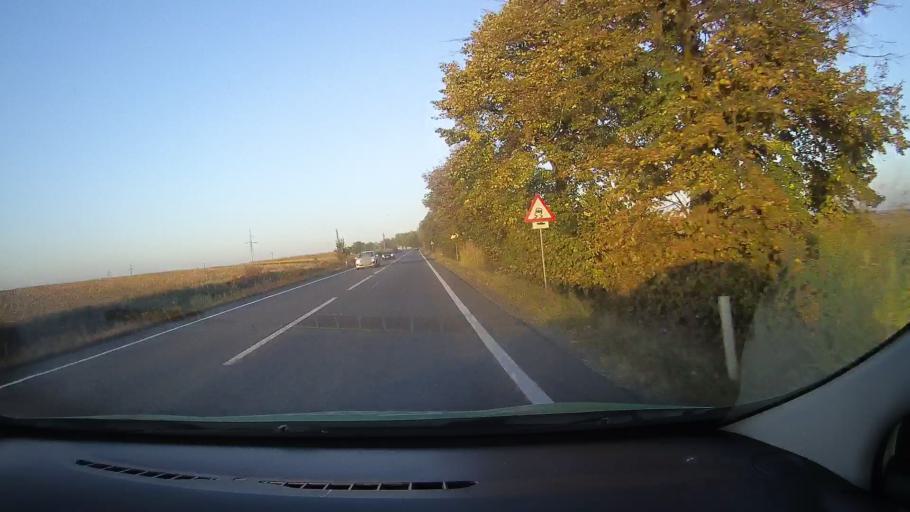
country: RO
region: Bihor
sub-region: Comuna Rosiori
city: Rosiori
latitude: 47.2636
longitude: 21.9688
